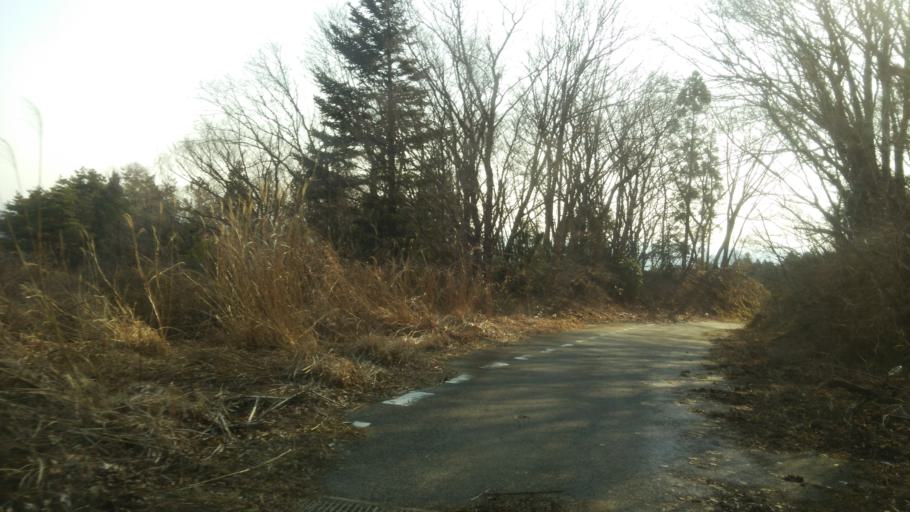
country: JP
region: Fukushima
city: Iwaki
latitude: 37.0383
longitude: 140.7956
